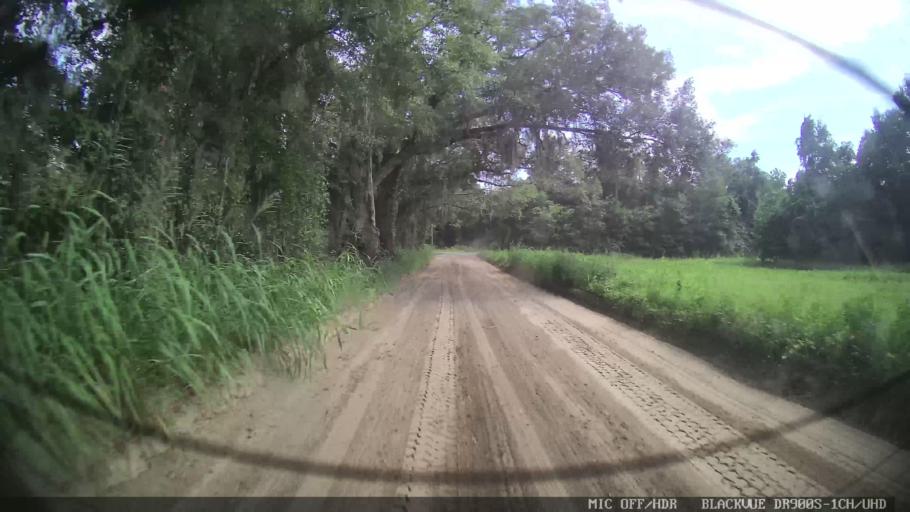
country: US
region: Florida
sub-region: Madison County
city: Madison
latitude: 30.5821
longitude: -83.2206
